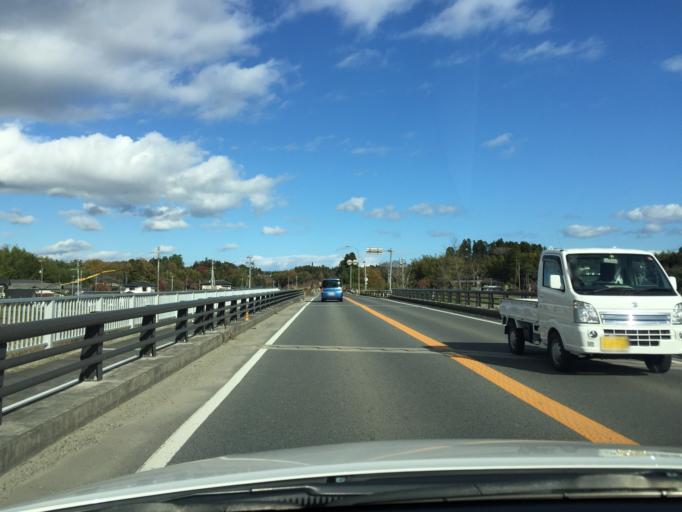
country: JP
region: Fukushima
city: Namie
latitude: 37.5653
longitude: 141.0029
